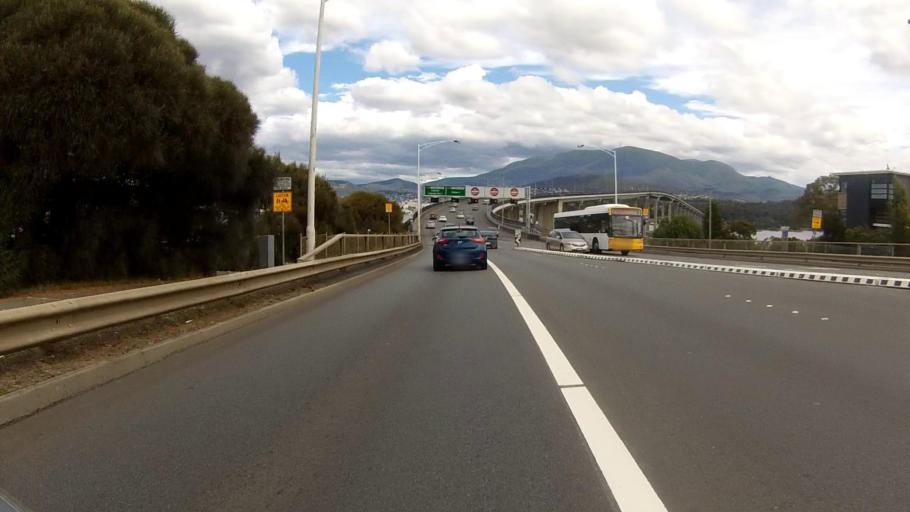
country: AU
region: Tasmania
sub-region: Clarence
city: Lindisfarne
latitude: -42.8628
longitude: 147.3535
